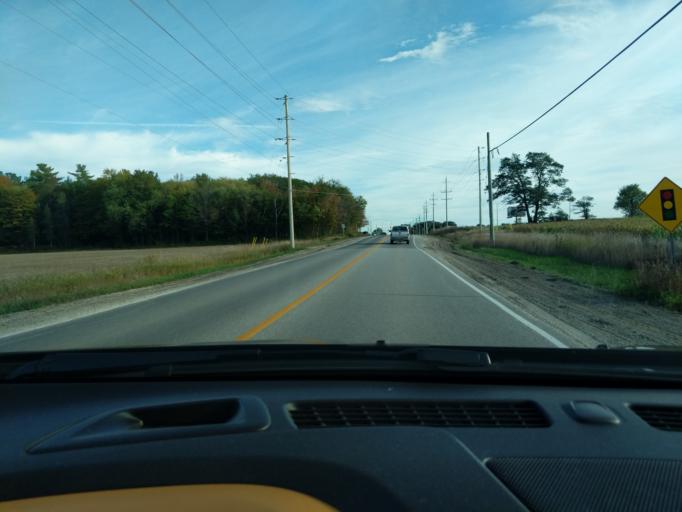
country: CA
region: Ontario
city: Barrie
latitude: 44.4025
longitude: -79.7431
